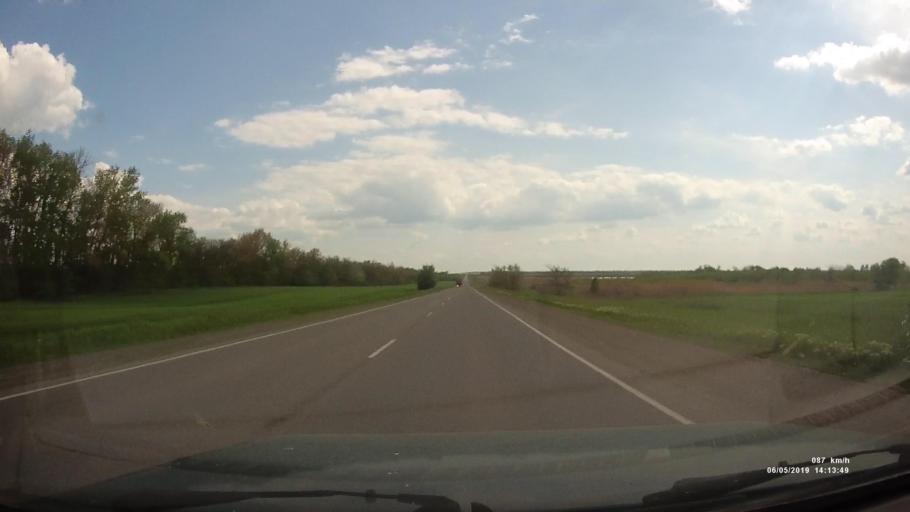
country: RU
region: Rostov
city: Kamenolomni
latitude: 47.6560
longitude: 40.2948
